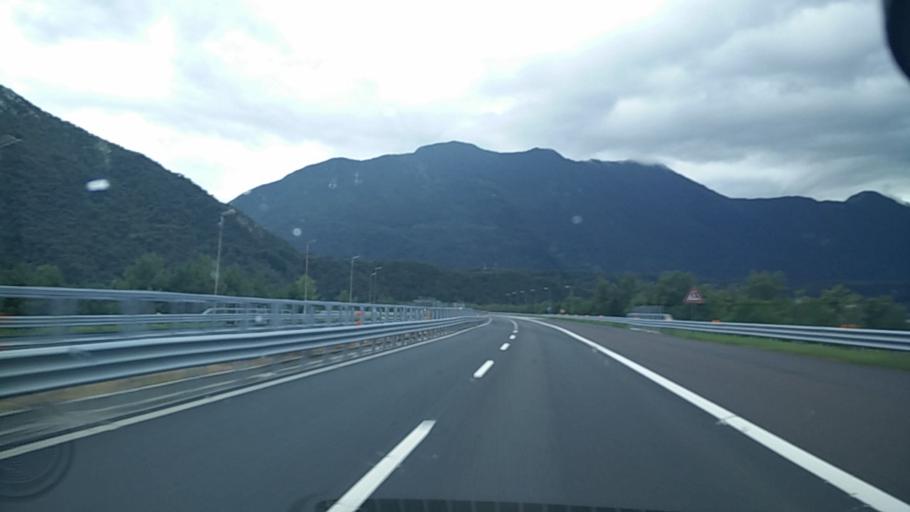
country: IT
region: Friuli Venezia Giulia
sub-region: Provincia di Udine
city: Amaro
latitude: 46.3664
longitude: 13.0797
